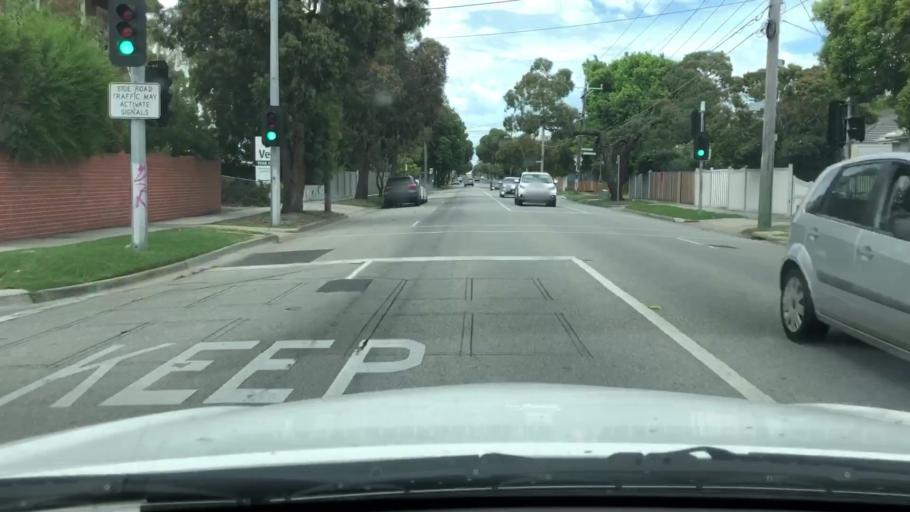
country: AU
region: Victoria
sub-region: Bayside
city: Black Rock
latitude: -37.9566
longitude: 145.0201
